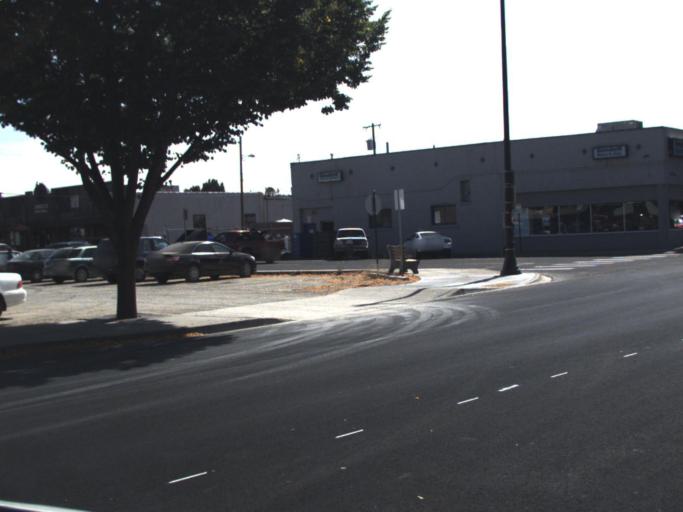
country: US
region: Washington
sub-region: Stevens County
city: Colville
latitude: 48.5457
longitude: -117.9058
